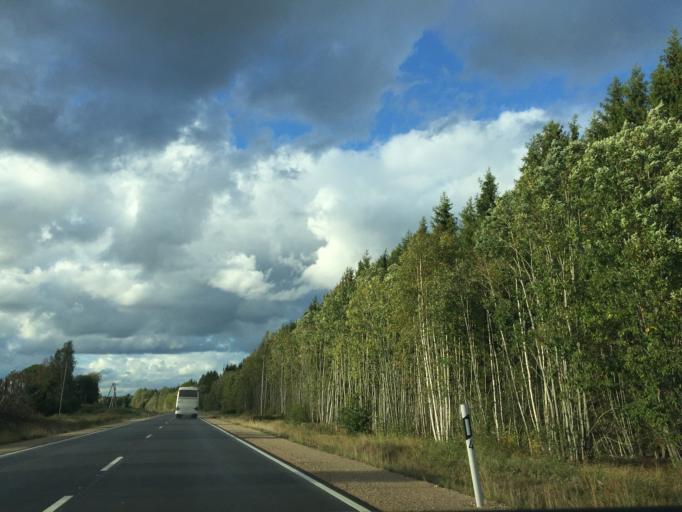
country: LV
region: Ligatne
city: Ligatne
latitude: 57.1414
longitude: 25.0803
